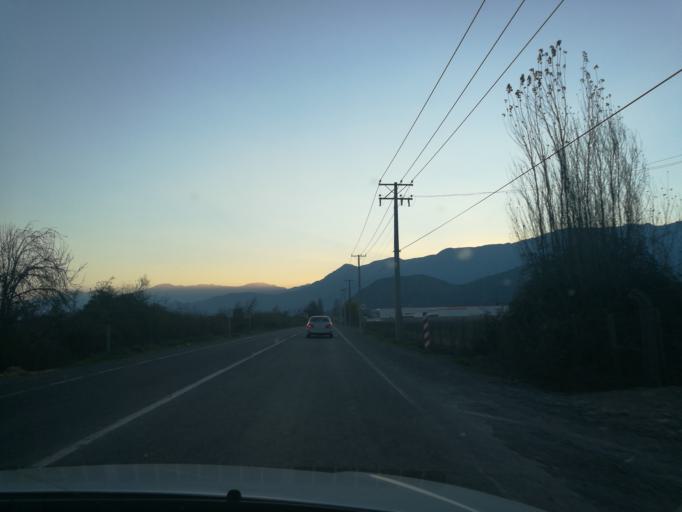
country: CL
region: O'Higgins
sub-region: Provincia de Cachapoal
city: Graneros
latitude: -34.0391
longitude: -70.6961
